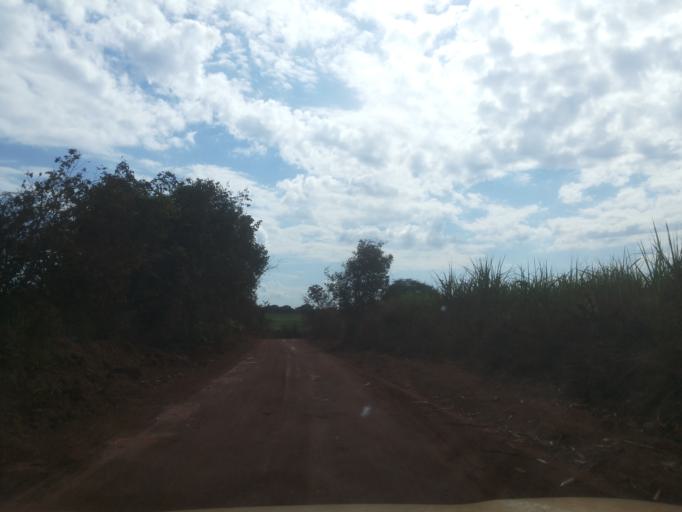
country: BR
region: Minas Gerais
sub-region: Ituiutaba
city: Ituiutaba
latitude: -19.0175
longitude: -49.3969
